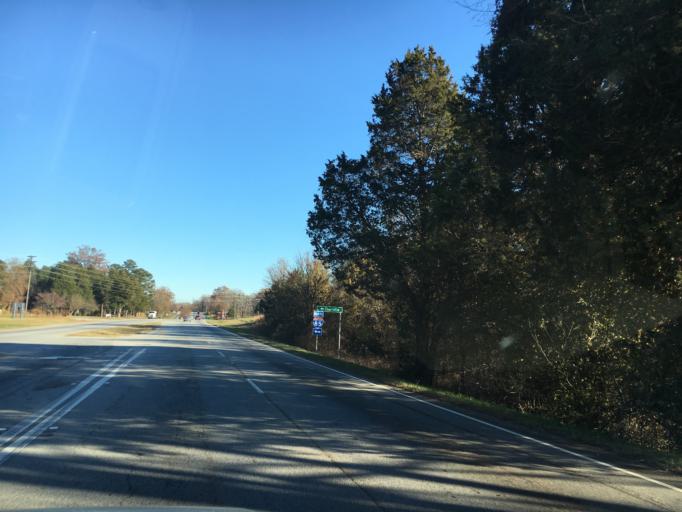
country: US
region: South Carolina
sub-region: Spartanburg County
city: Wellford
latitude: 34.9391
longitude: -82.0747
